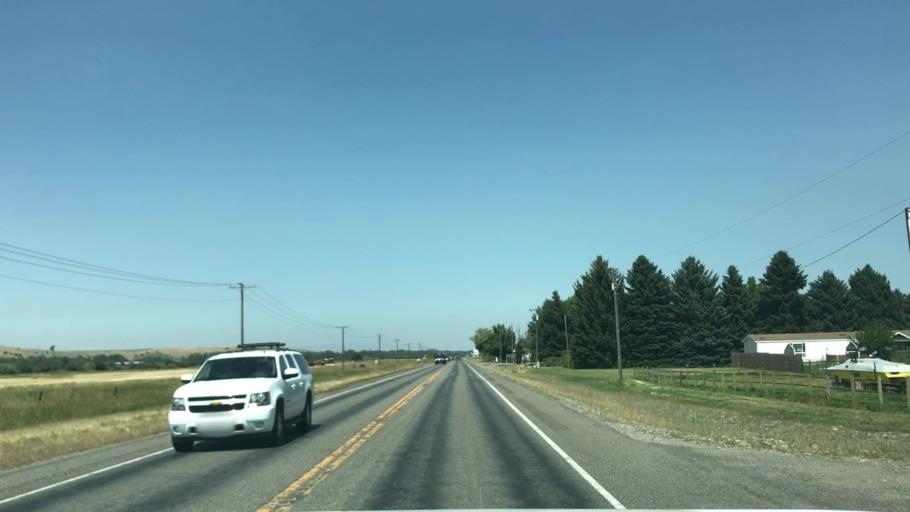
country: US
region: Montana
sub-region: Gallatin County
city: Four Corners
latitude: 45.6252
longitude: -111.1969
